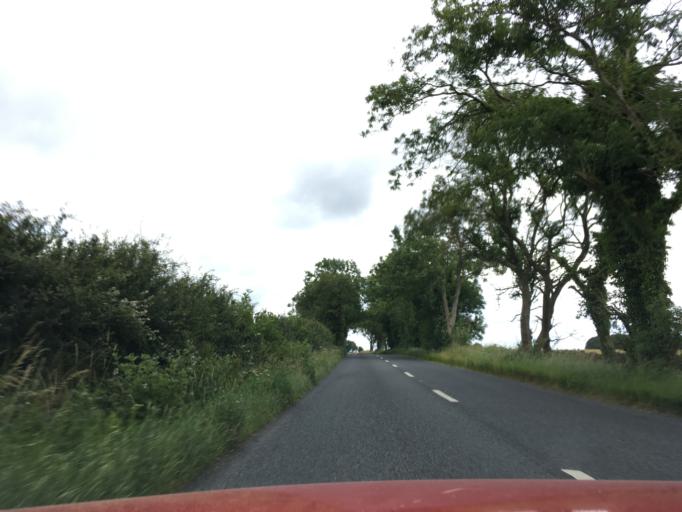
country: GB
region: England
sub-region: Gloucestershire
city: Westfield
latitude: 51.8891
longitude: -1.8591
